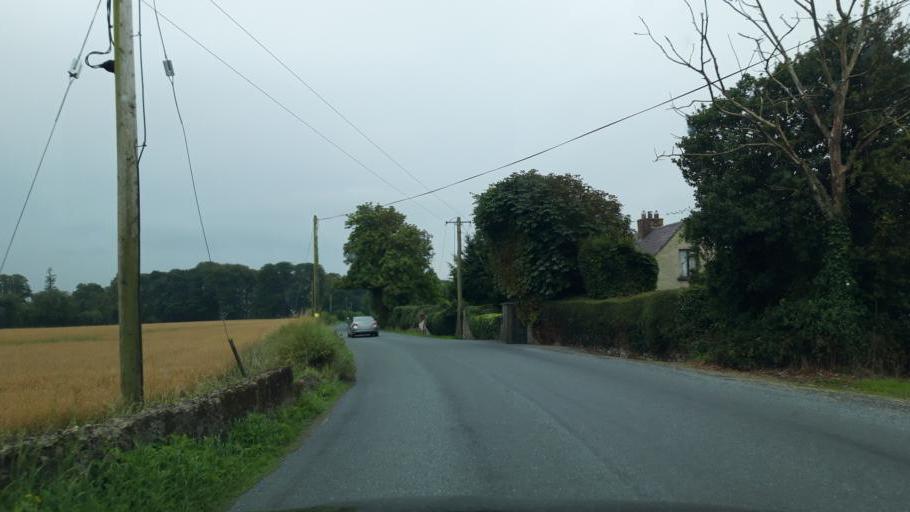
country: IE
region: Munster
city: Fethard
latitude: 52.4418
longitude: -7.7023
